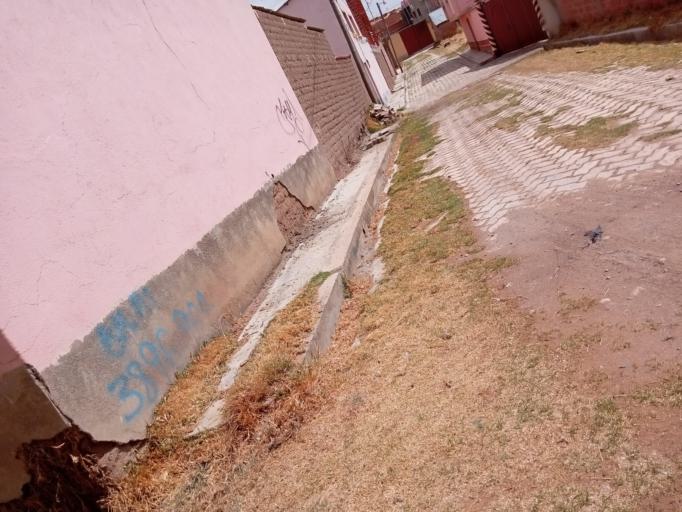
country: BO
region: La Paz
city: Batallas
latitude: -16.3997
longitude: -68.4792
